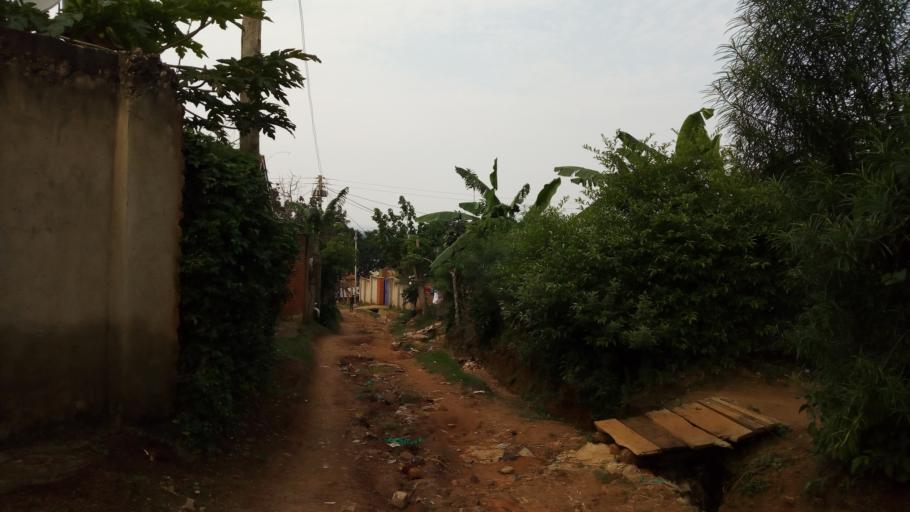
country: UG
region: Central Region
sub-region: Wakiso District
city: Kireka
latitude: 0.3129
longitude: 32.6482
